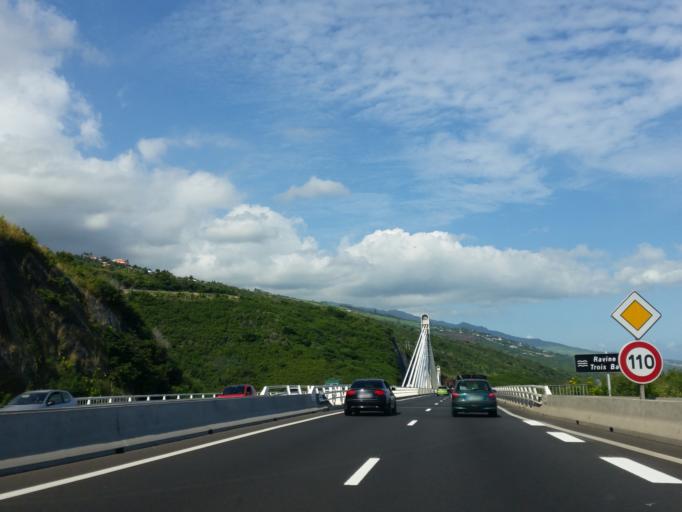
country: RE
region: Reunion
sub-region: Reunion
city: Trois-Bassins
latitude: -21.1039
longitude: 55.2706
